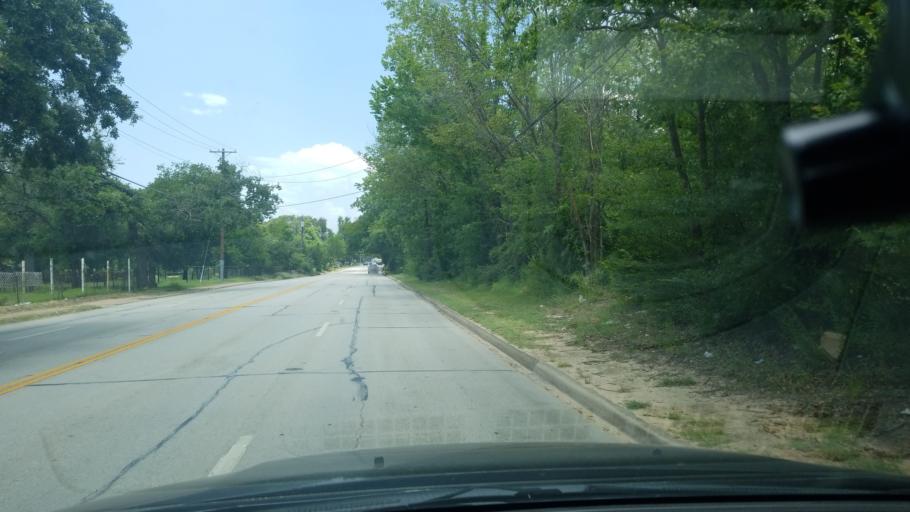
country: US
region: Texas
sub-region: Dallas County
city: Balch Springs
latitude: 32.7155
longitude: -96.6571
